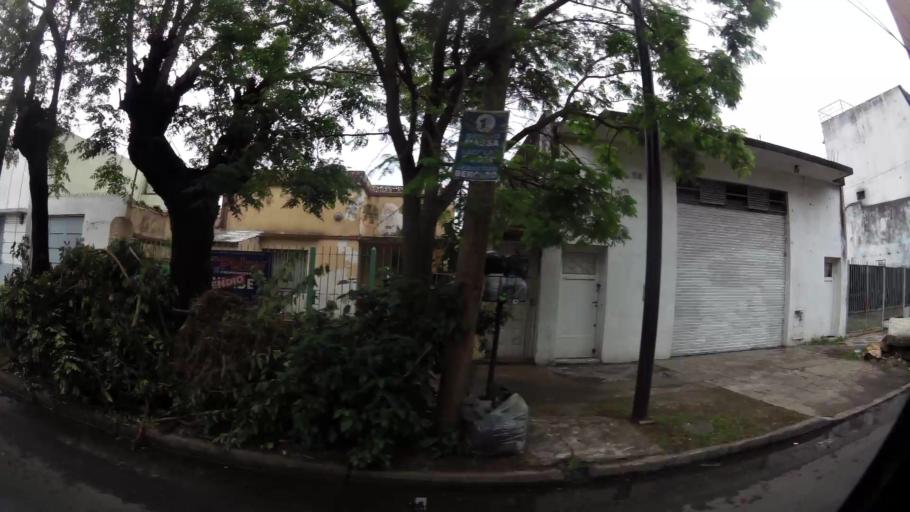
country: AR
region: Buenos Aires
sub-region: Partido de Lanus
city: Lanus
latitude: -34.7132
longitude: -58.3896
